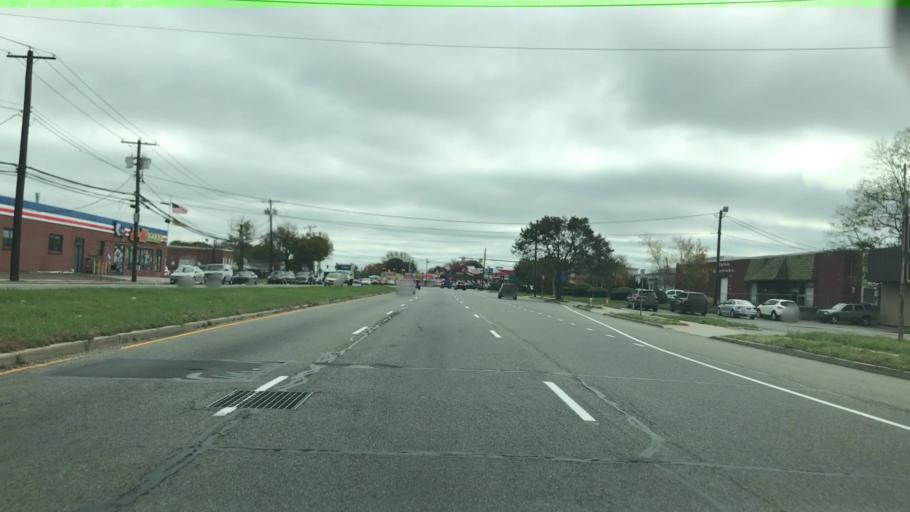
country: US
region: New York
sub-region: Suffolk County
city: North Lindenhurst
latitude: 40.7163
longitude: -73.3962
